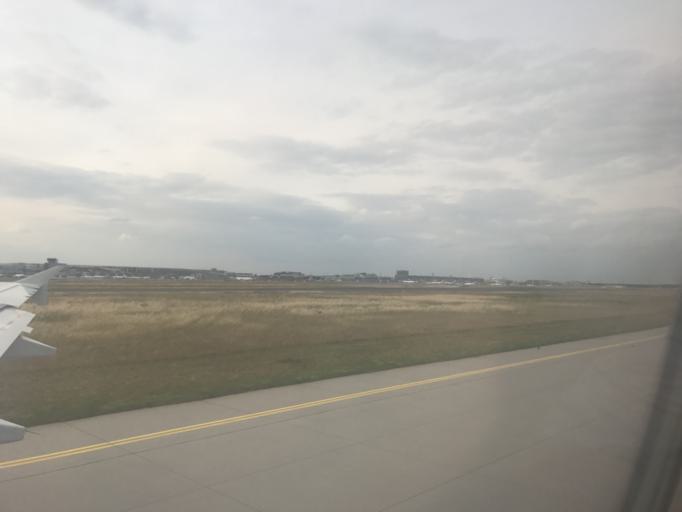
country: DE
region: Hesse
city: Morfelden-Walldorf
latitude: 50.0331
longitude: 8.5695
